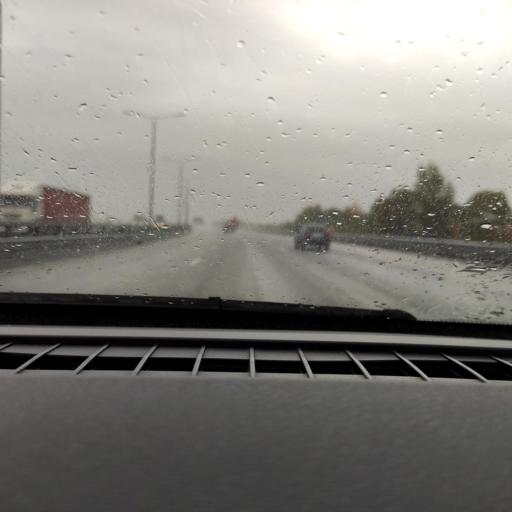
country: RU
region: Voronezj
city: Somovo
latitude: 51.7970
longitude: 39.2578
